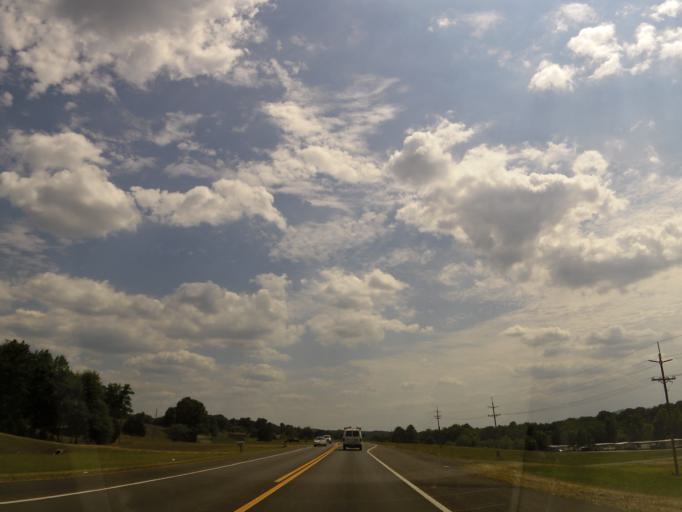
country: US
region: Tennessee
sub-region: Marion County
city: Whitwell
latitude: 35.1602
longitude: -85.5386
